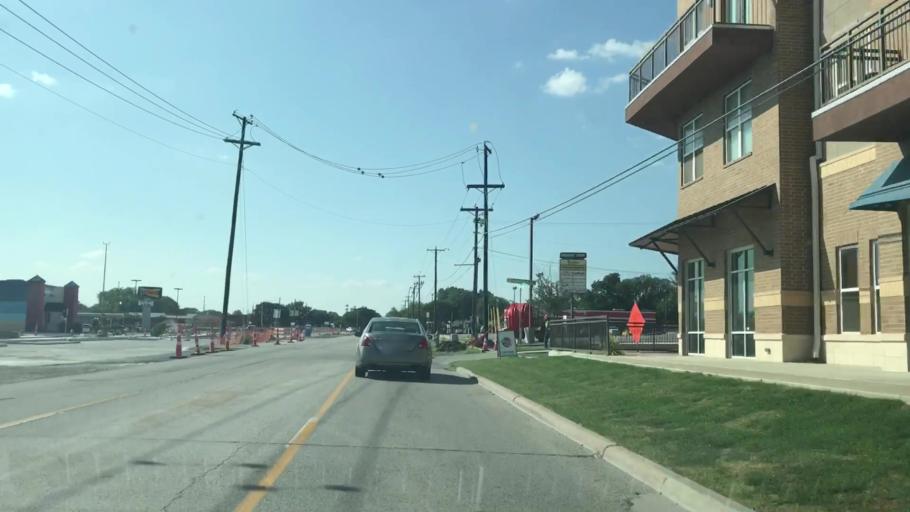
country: US
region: Texas
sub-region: Dallas County
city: Mesquite
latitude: 32.8246
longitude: -96.6473
